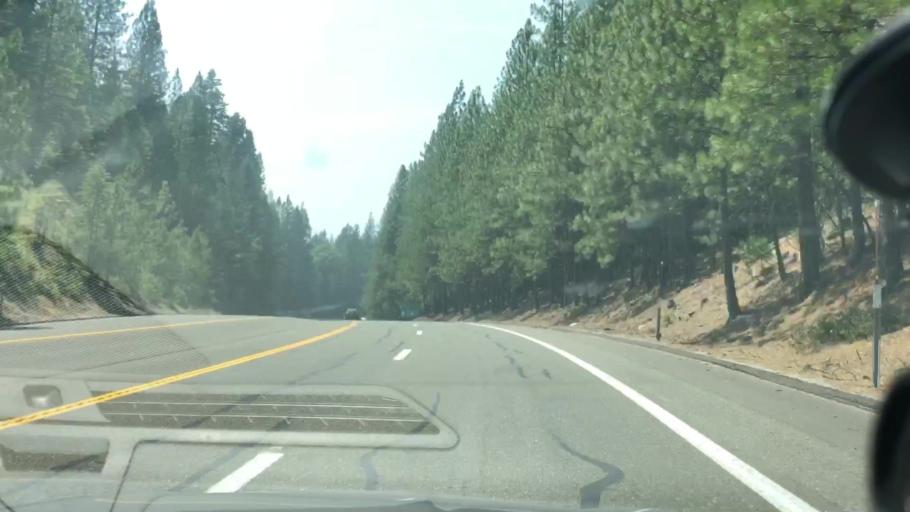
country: US
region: California
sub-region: El Dorado County
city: Pollock Pines
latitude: 38.7610
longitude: -120.5239
